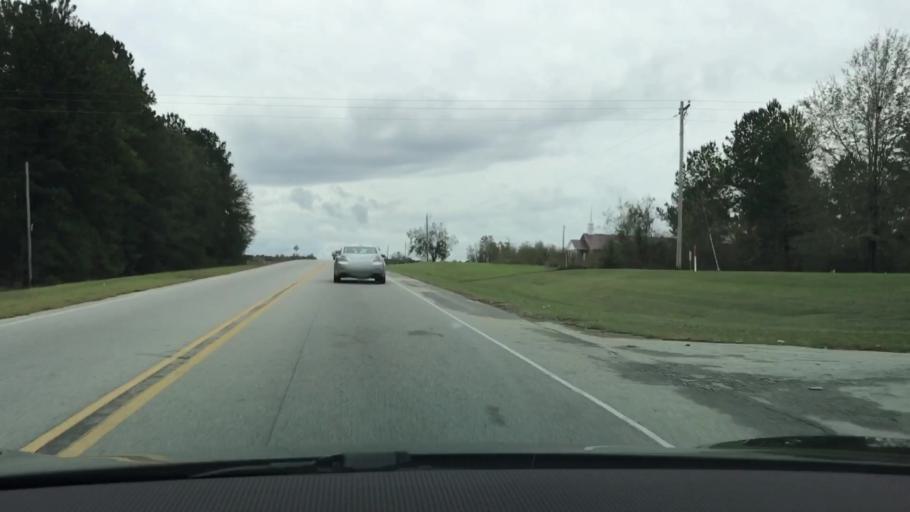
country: US
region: Georgia
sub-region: Jefferson County
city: Louisville
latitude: 32.9508
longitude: -82.3945
